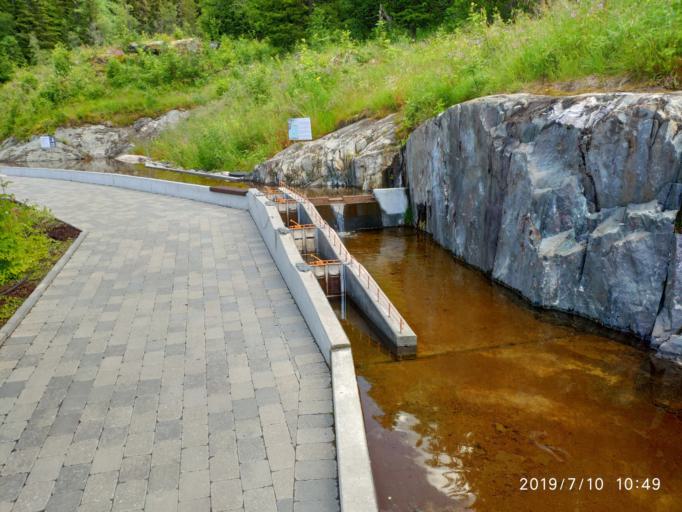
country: NO
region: Telemark
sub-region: Tokke
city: Dalen
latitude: 59.4660
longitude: 8.0205
